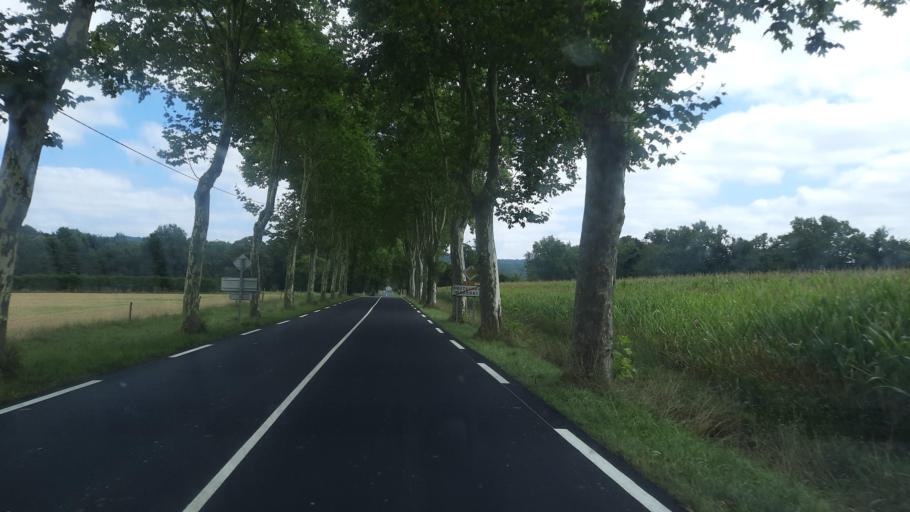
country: FR
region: Midi-Pyrenees
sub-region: Departement de la Haute-Garonne
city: Boulogne-sur-Gesse
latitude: 43.2907
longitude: 0.5274
